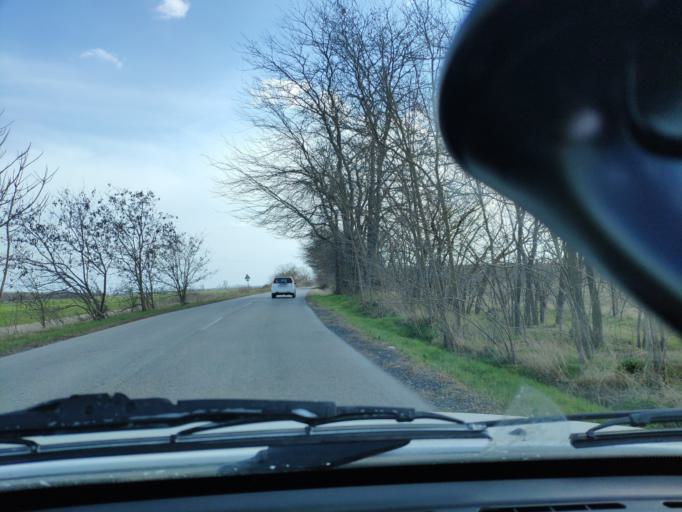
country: HU
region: Pest
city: Rackeve
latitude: 47.1455
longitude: 18.9113
